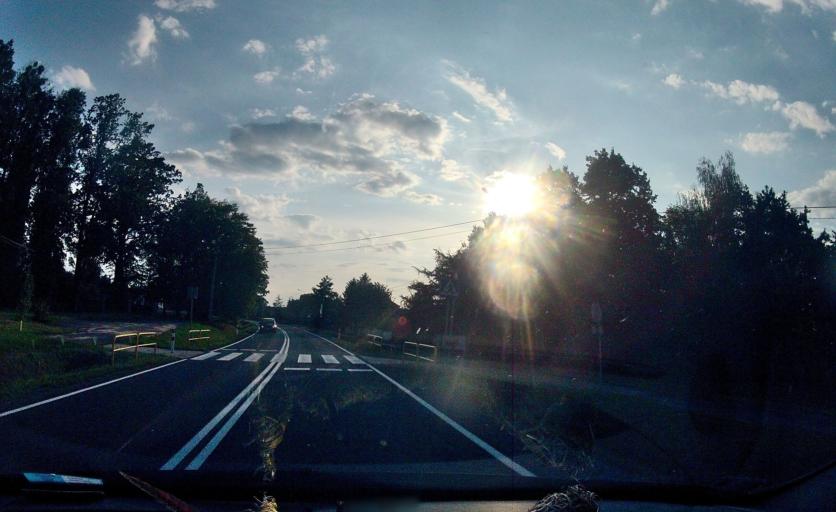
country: PL
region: Opole Voivodeship
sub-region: Powiat kluczborski
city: Kluczbork
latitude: 51.0019
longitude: 18.3177
